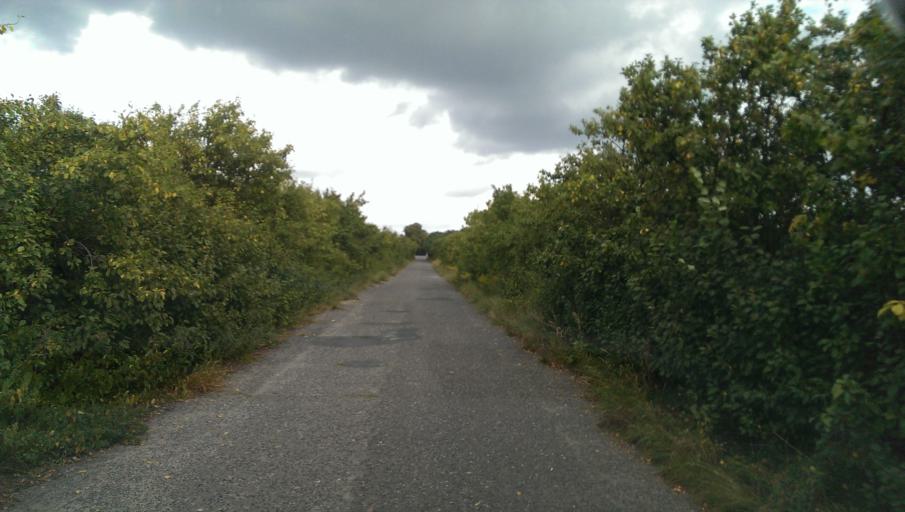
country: DE
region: Brandenburg
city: Rangsdorf
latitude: 52.3021
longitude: 13.4775
